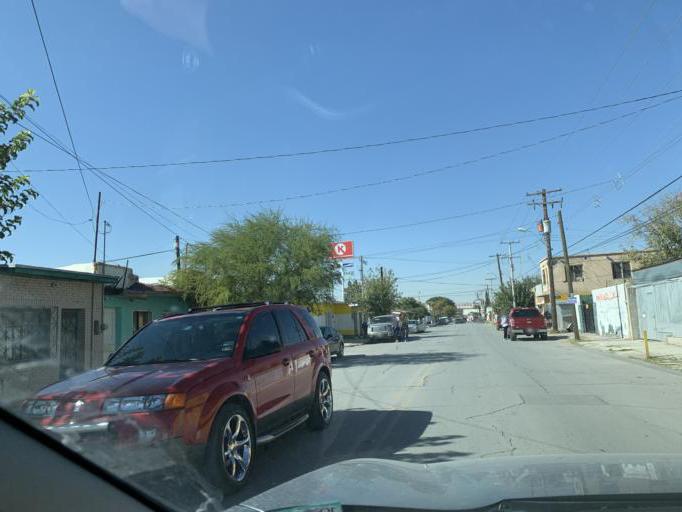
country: MX
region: Chihuahua
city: Ciudad Juarez
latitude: 31.7244
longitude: -106.4610
